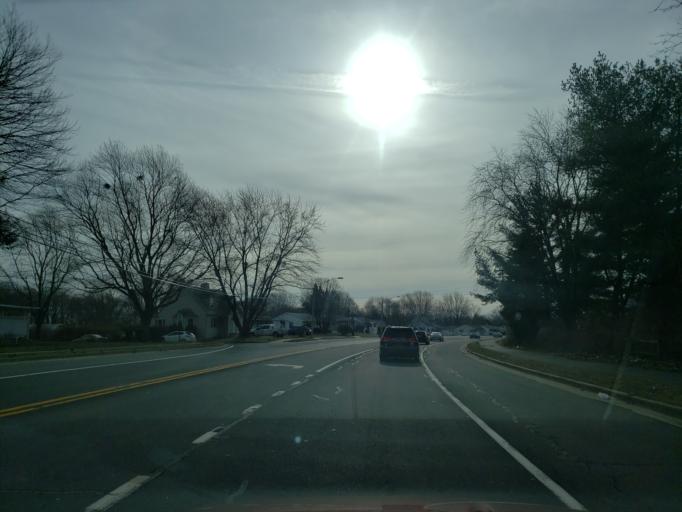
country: US
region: Delaware
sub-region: Kent County
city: Dover
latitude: 39.1728
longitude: -75.5484
